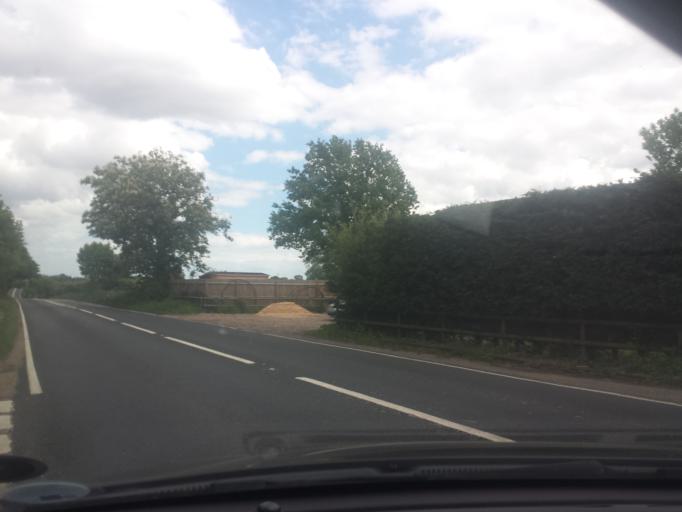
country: GB
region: England
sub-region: Essex
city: Little Clacton
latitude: 51.8607
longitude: 1.1401
